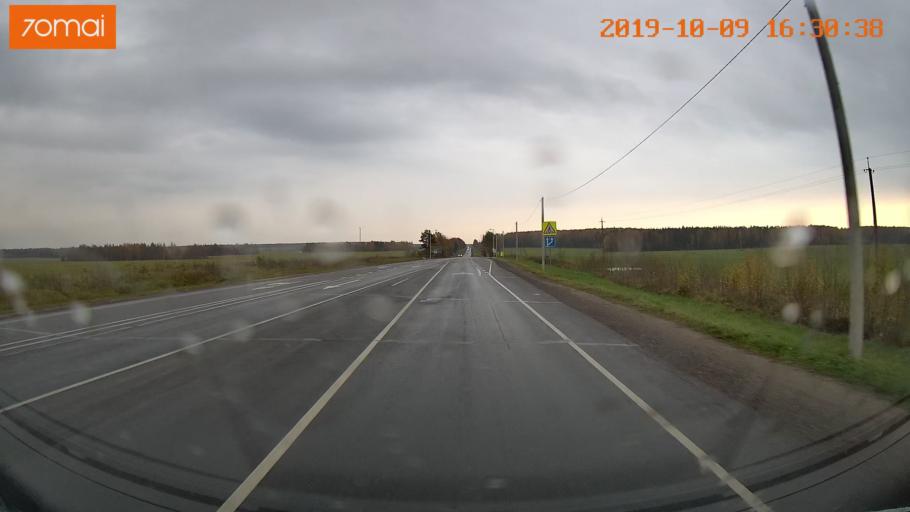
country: RU
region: Kostroma
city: Oktyabr'skiy
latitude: 57.6168
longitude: 40.9423
